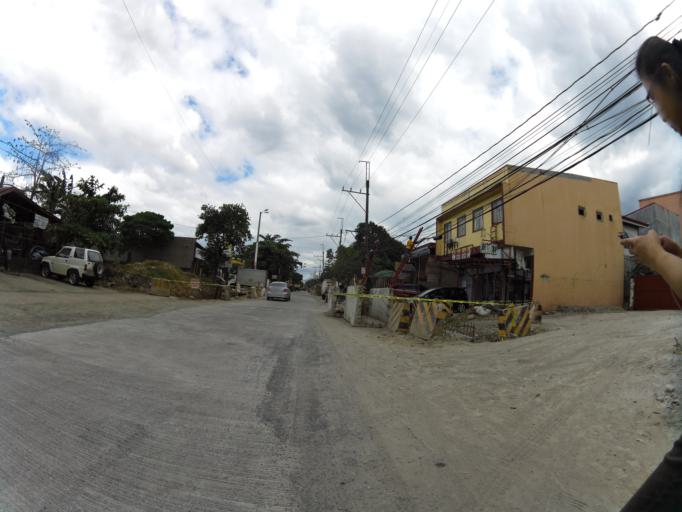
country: PH
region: Calabarzon
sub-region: Province of Rizal
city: Antipolo
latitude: 14.6402
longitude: 121.1099
